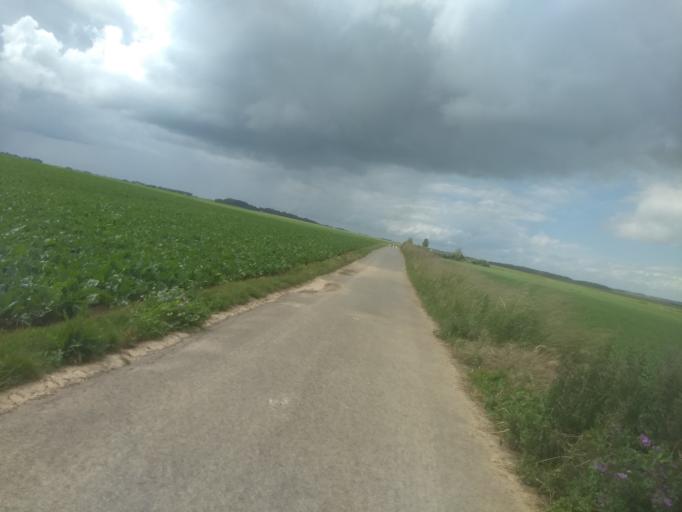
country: FR
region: Nord-Pas-de-Calais
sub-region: Departement du Pas-de-Calais
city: Dainville
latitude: 50.2598
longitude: 2.7092
